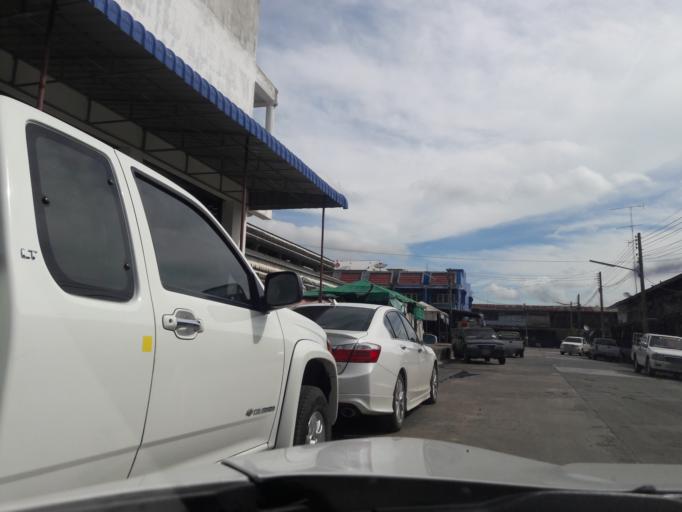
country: TH
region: Nakhon Sawan
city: Tak Fa
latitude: 15.3454
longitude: 100.4954
